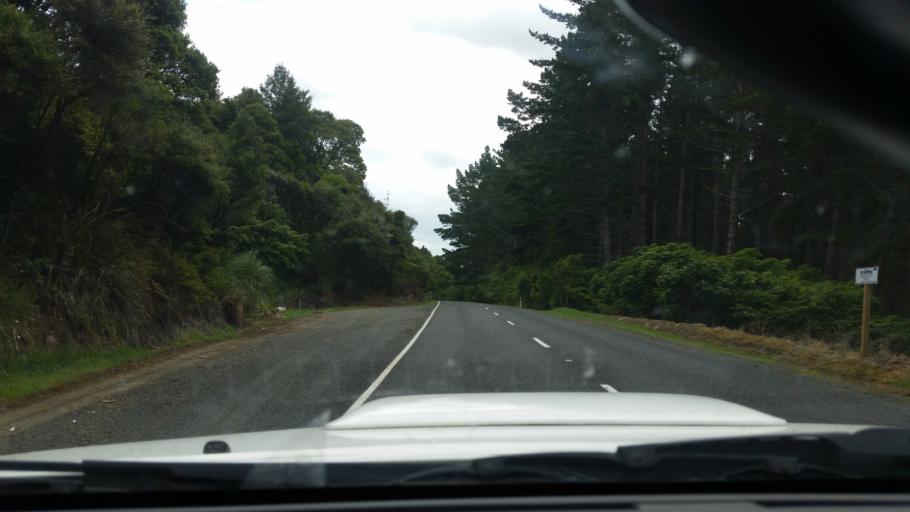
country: NZ
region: Northland
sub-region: Kaipara District
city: Dargaville
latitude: -35.7343
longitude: 173.8644
